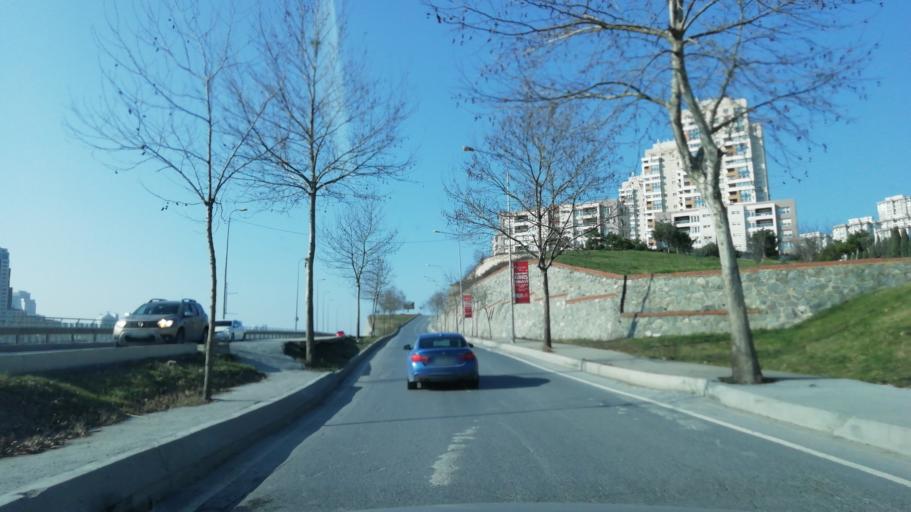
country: TR
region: Istanbul
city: Esenyurt
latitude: 41.0750
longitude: 28.6913
